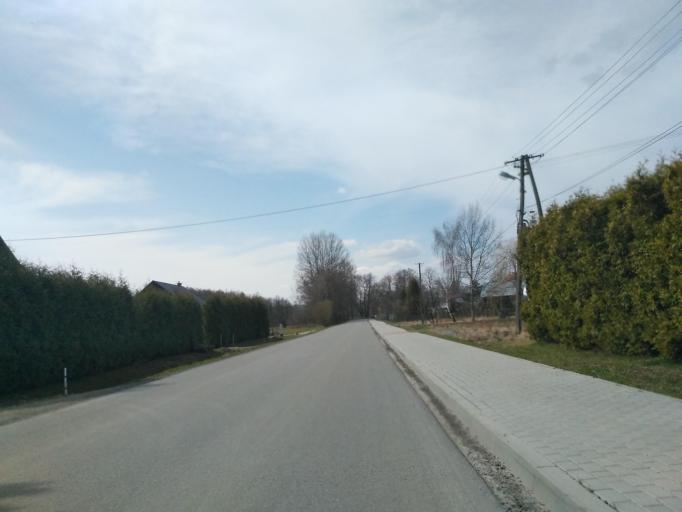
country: PL
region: Subcarpathian Voivodeship
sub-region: Powiat ropczycko-sedziszowski
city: Iwierzyce
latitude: 50.0207
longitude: 21.7971
